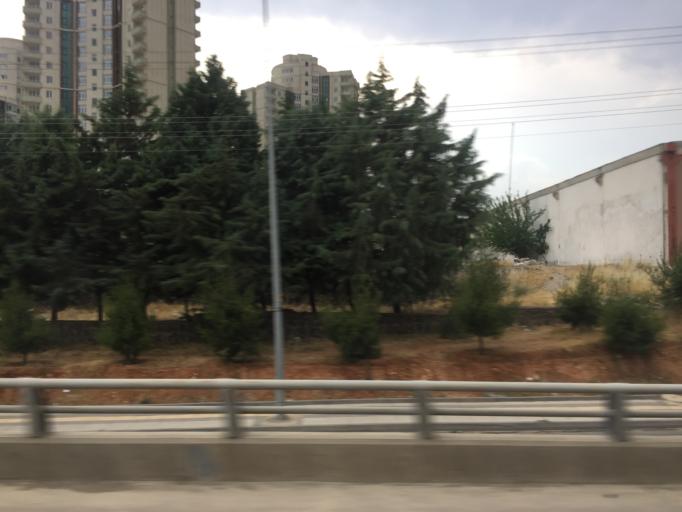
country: TR
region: Gaziantep
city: Gaziantep
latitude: 37.0386
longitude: 37.4237
